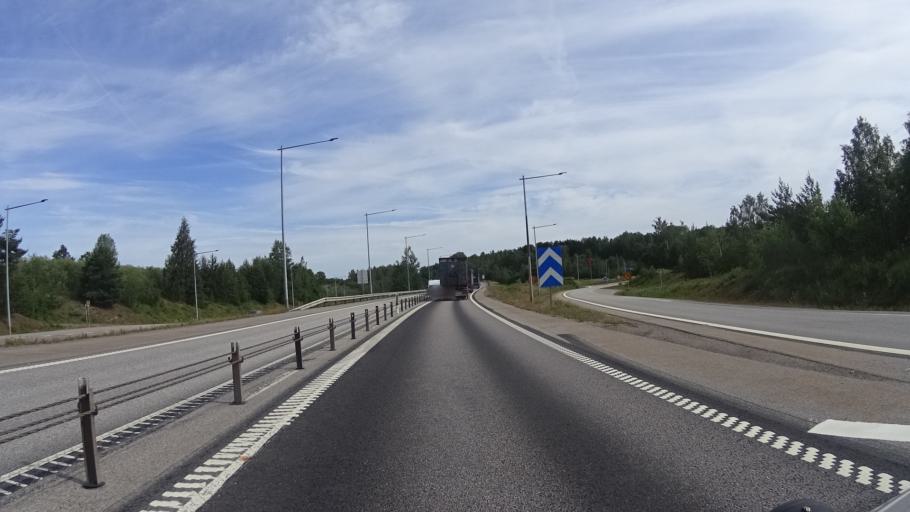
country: SE
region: Kalmar
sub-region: Vasterviks Kommun
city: Vaestervik
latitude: 57.7611
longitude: 16.5565
